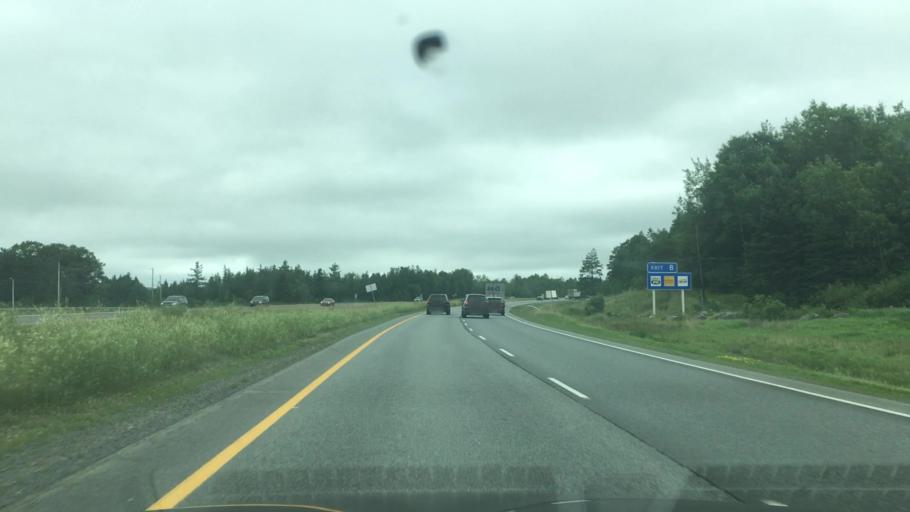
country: CA
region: Nova Scotia
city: Dartmouth
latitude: 44.9530
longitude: -63.5396
